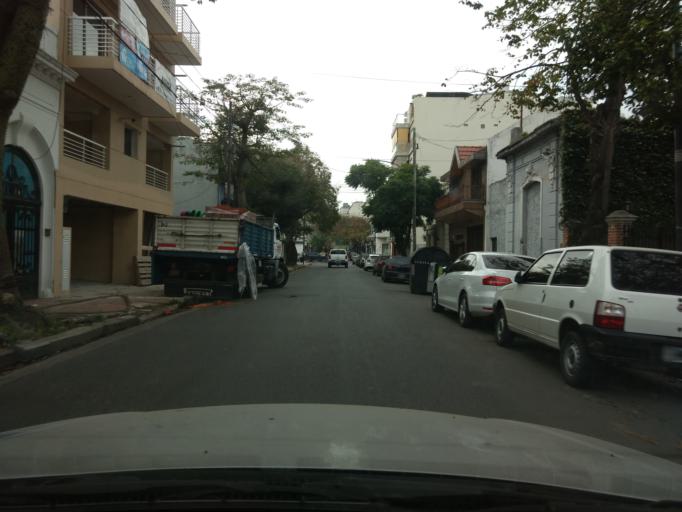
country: AR
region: Buenos Aires F.D.
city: Villa Santa Rita
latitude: -34.6202
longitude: -58.4708
